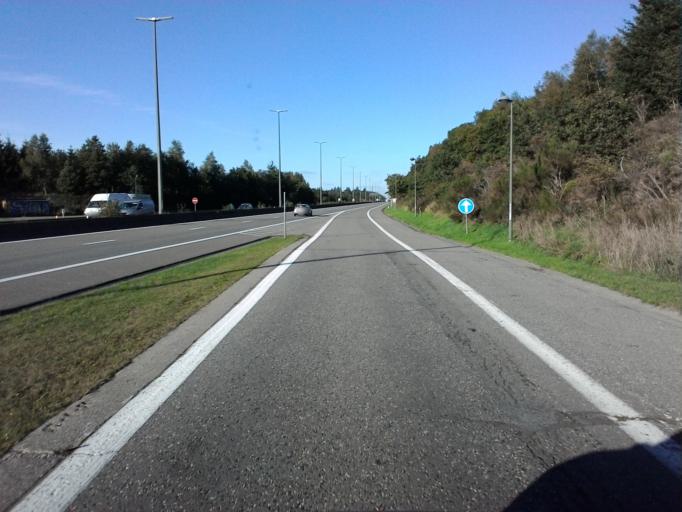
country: BE
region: Wallonia
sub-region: Province du Luxembourg
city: Bastogne
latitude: 50.0445
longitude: 5.7110
